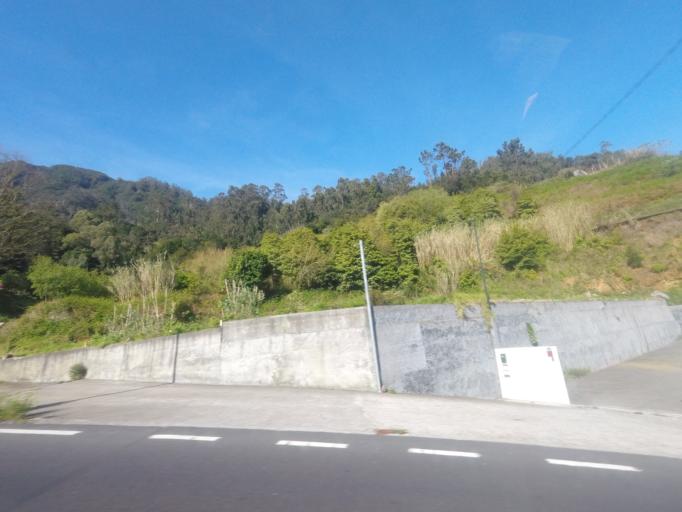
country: PT
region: Madeira
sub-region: Sao Vicente
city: Sao Vicente
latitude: 32.7761
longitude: -17.0330
